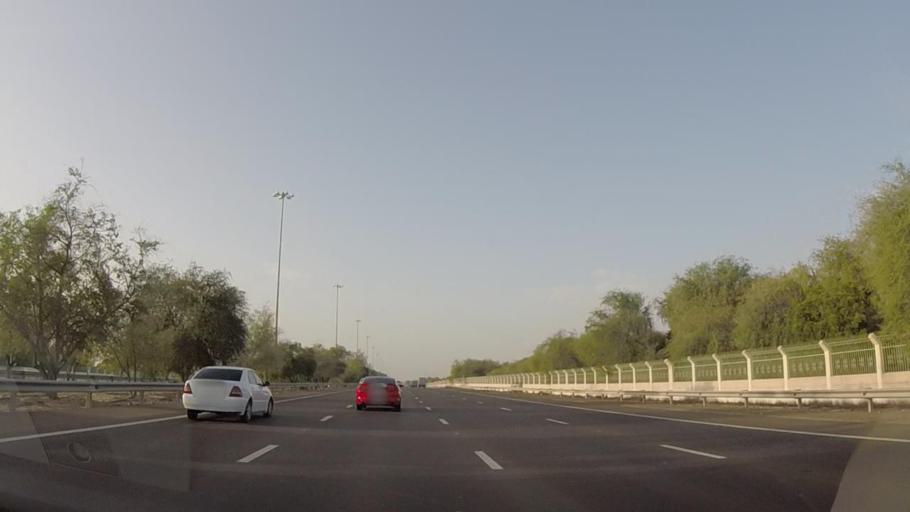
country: AE
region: Dubai
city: Dubai
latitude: 24.8274
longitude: 54.8805
